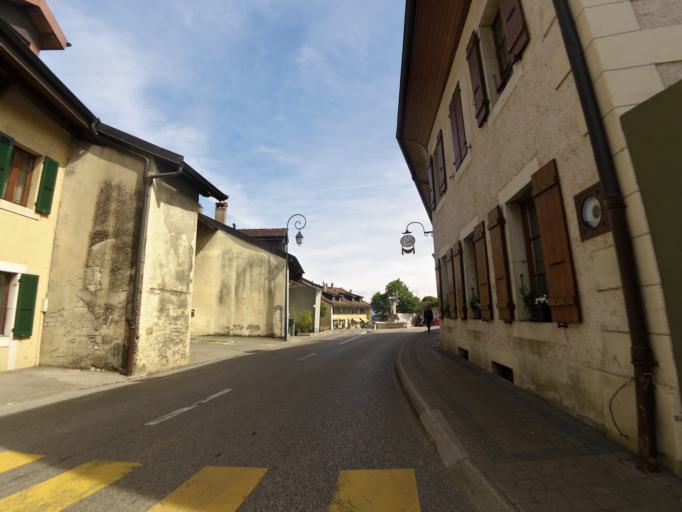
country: CH
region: Vaud
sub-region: Nyon District
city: Genolier
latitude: 46.4353
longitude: 6.2174
